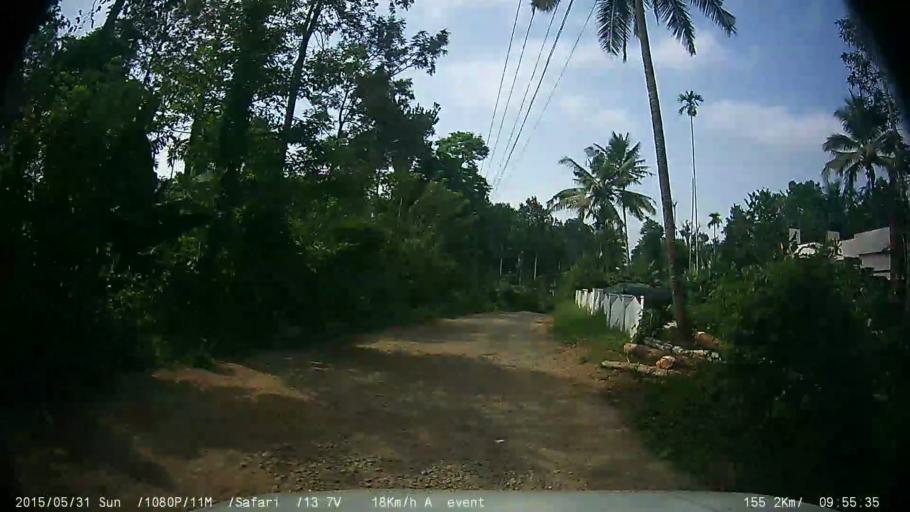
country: IN
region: Kerala
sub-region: Wayanad
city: Kalpetta
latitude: 11.6018
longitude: 76.0540
